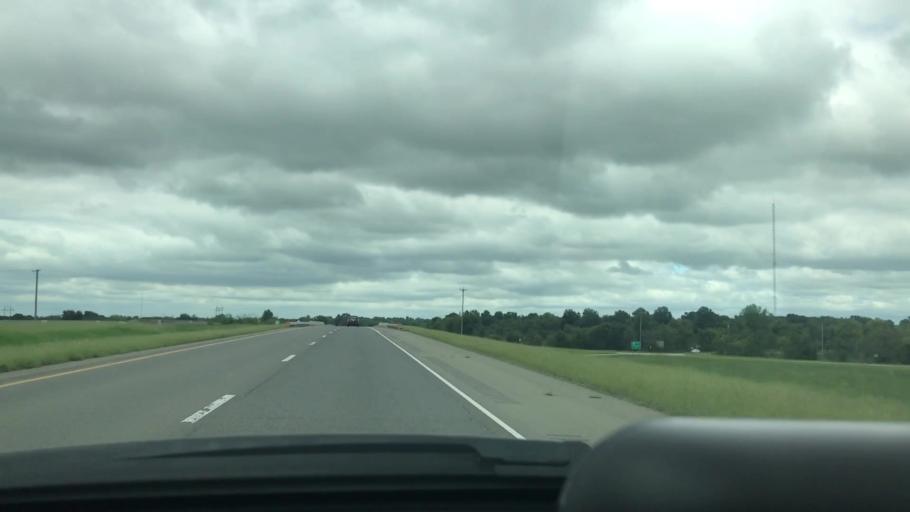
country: US
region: Oklahoma
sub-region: McIntosh County
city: Checotah
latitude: 35.5748
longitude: -95.4909
